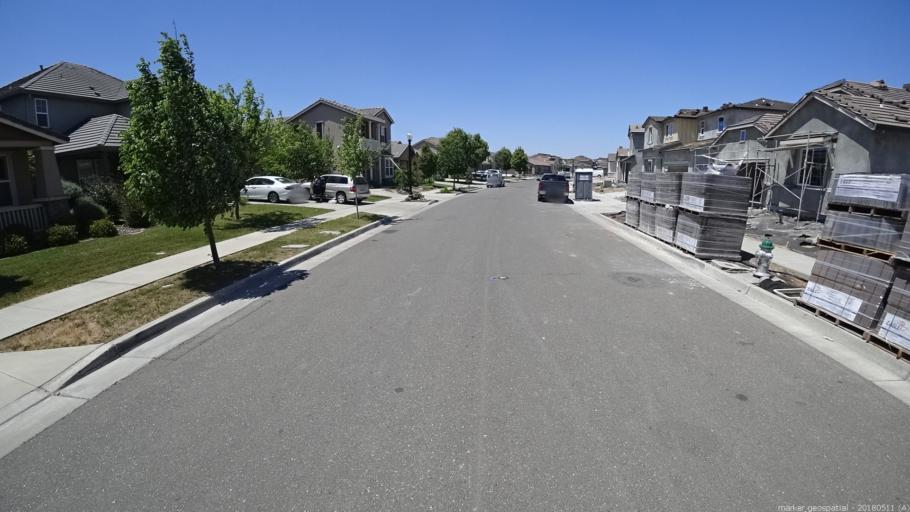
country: US
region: California
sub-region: Yolo County
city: West Sacramento
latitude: 38.6447
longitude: -121.5504
